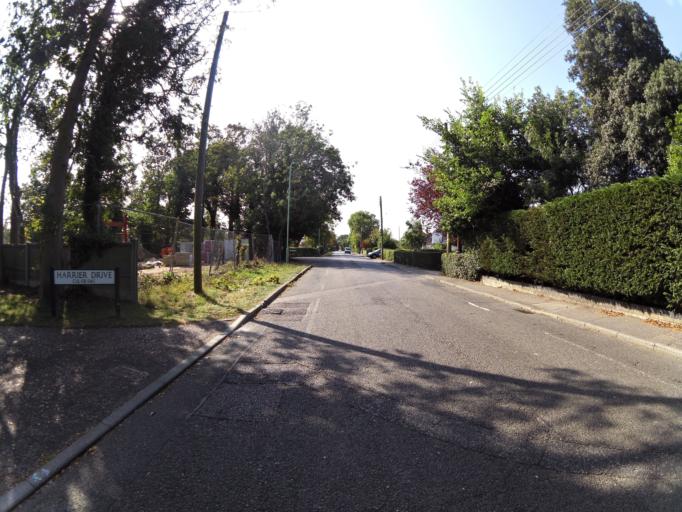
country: GB
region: England
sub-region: Suffolk
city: Kessingland
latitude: 52.4631
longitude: 1.7080
